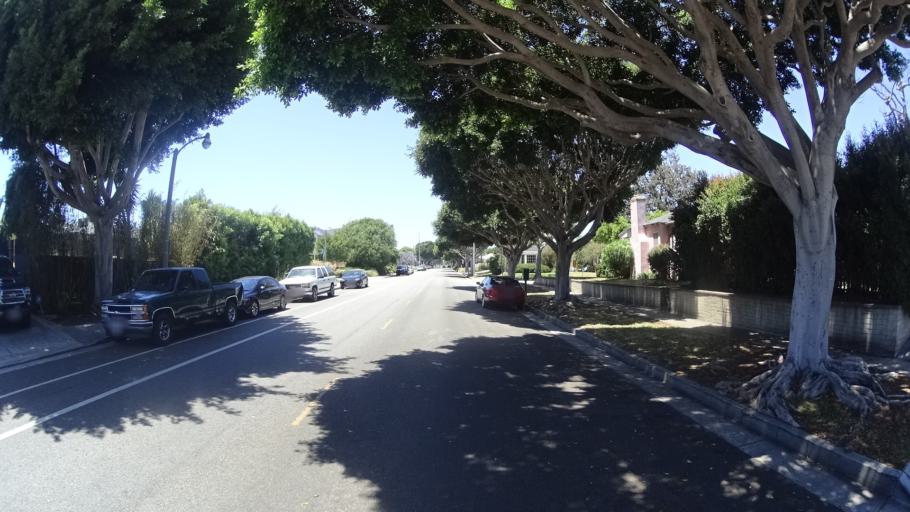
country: US
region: California
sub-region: Los Angeles County
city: Santa Monica
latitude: 34.0086
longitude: -118.4683
